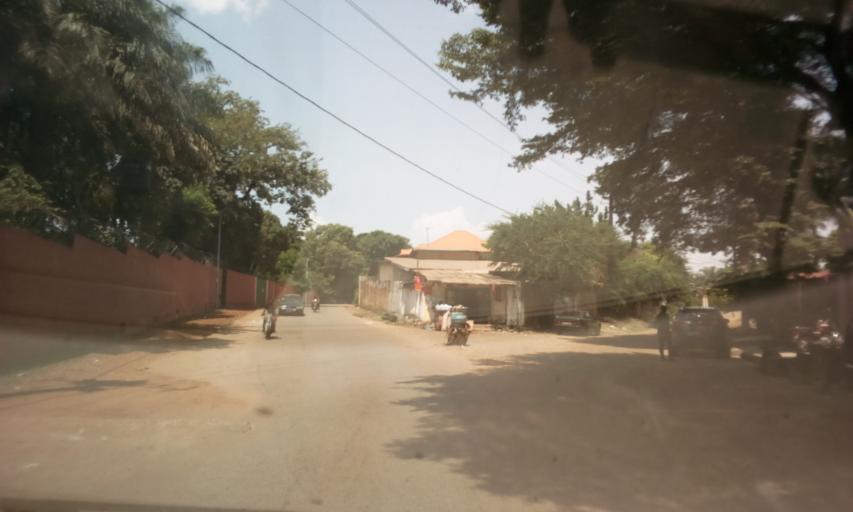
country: GN
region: Conakry
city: Conakry
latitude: 9.5676
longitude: -13.6650
